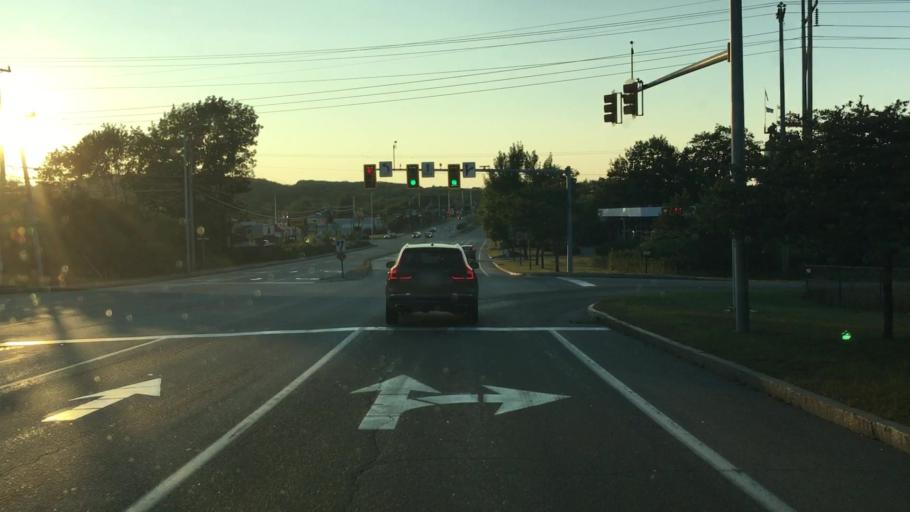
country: US
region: Maine
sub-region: Sagadahoc County
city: Topsham
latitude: 43.9387
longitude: -69.9731
